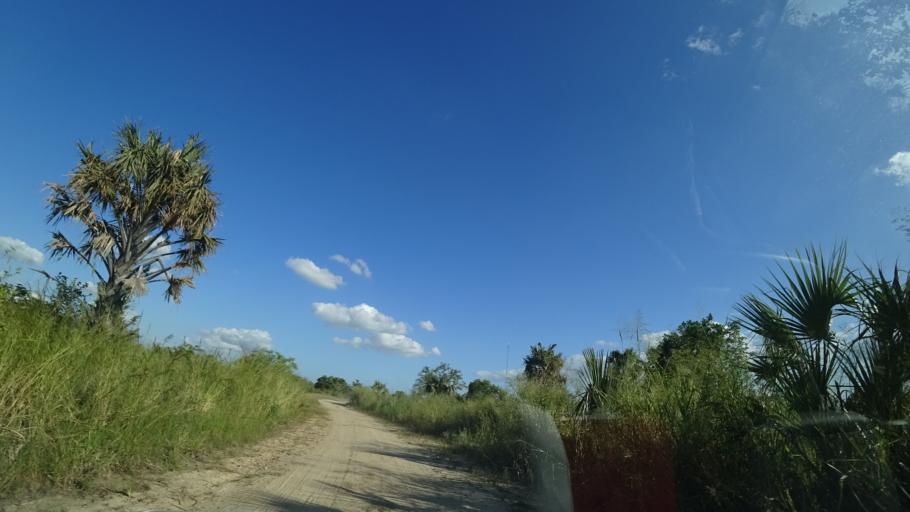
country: MZ
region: Sofala
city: Dondo
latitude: -19.3753
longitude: 34.5921
